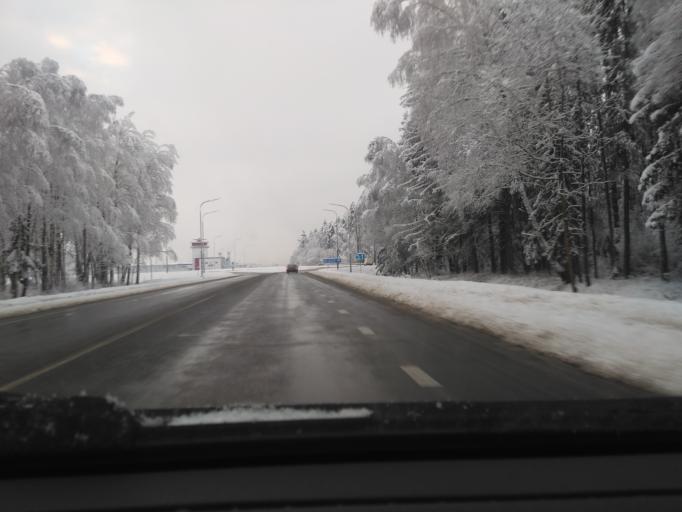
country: BY
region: Minsk
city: Horad Zhodzina
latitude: 54.1414
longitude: 28.3867
